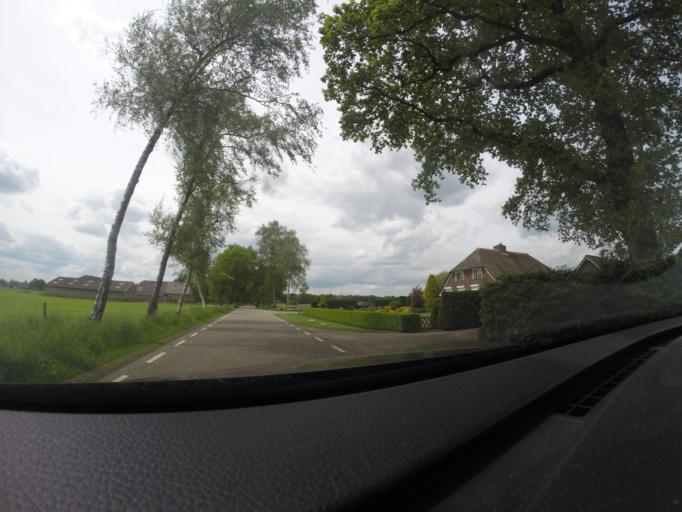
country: NL
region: Overijssel
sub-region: Gemeente Raalte
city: Raalte
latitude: 52.3049
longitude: 6.3019
